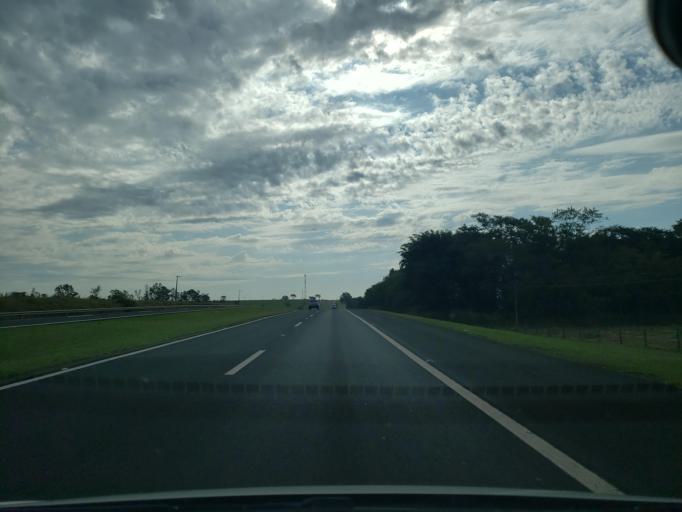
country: BR
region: Sao Paulo
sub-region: Birigui
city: Birigui
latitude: -21.3465
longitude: -50.3171
